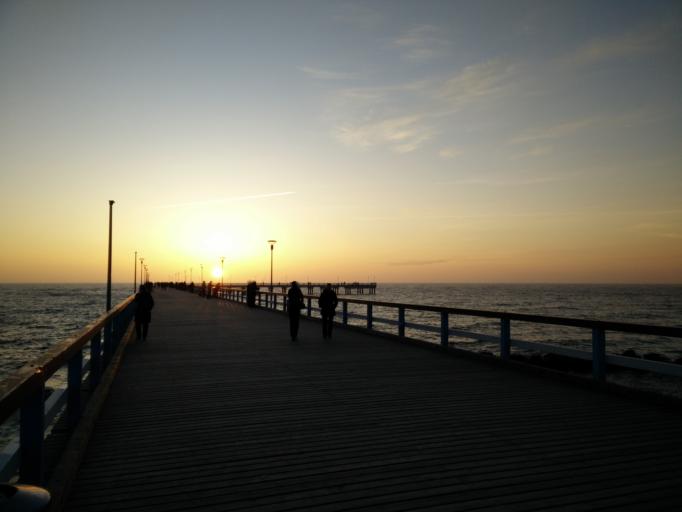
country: LT
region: Klaipedos apskritis
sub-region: Klaipeda
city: Palanga
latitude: 55.9200
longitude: 21.0484
